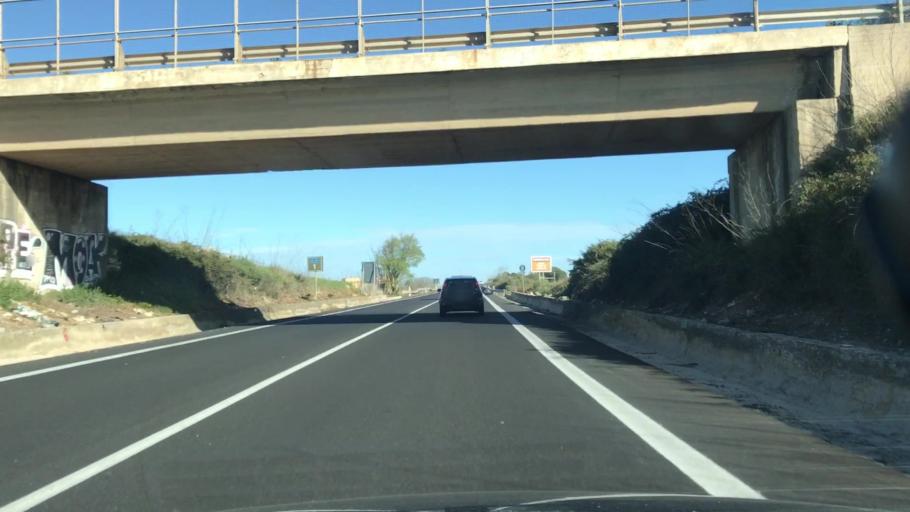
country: IT
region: Sicily
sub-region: Ragusa
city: Comiso
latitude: 36.9334
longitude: 14.6532
